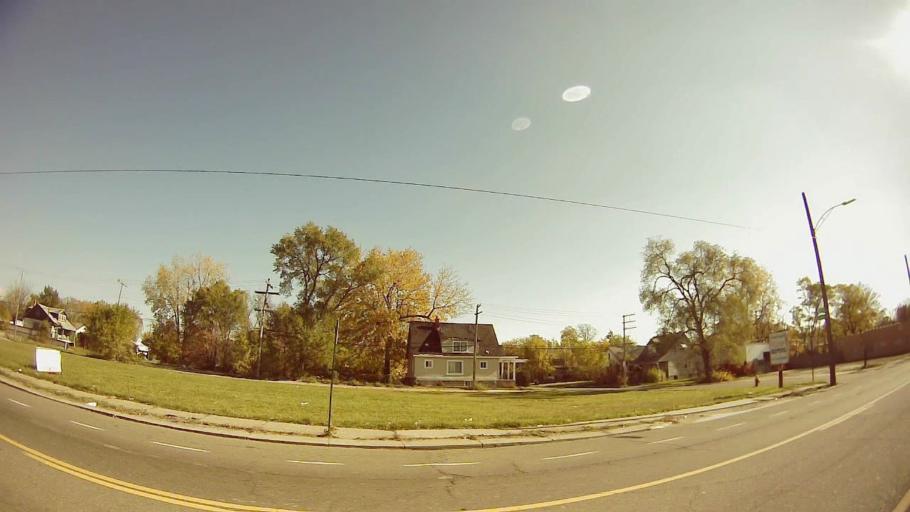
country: US
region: Michigan
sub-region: Oakland County
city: Oak Park
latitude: 42.4013
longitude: -83.1598
